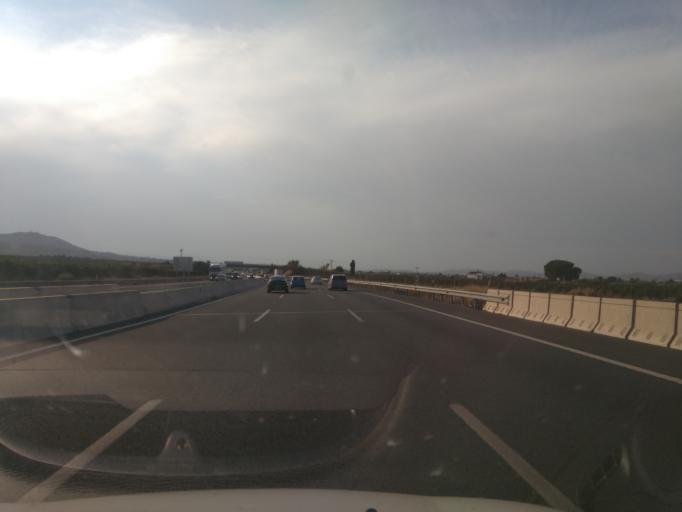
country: ES
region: Valencia
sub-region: Provincia de Valencia
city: Torrent
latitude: 39.4212
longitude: -0.5148
